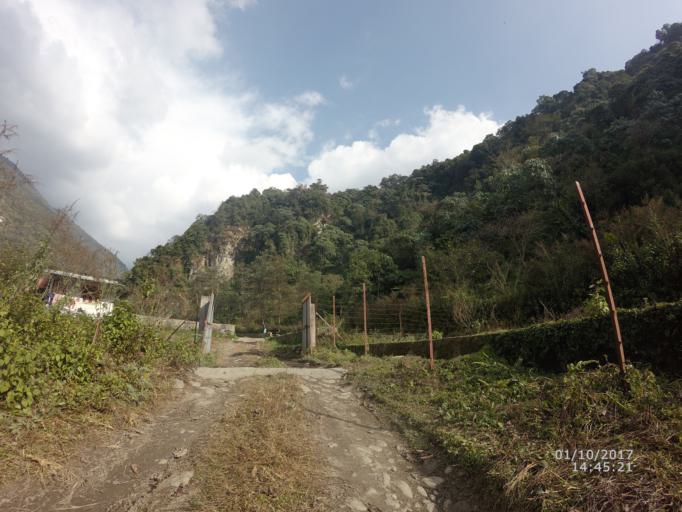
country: NP
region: Western Region
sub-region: Gandaki Zone
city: Pokhara
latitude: 28.3450
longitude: 83.9787
